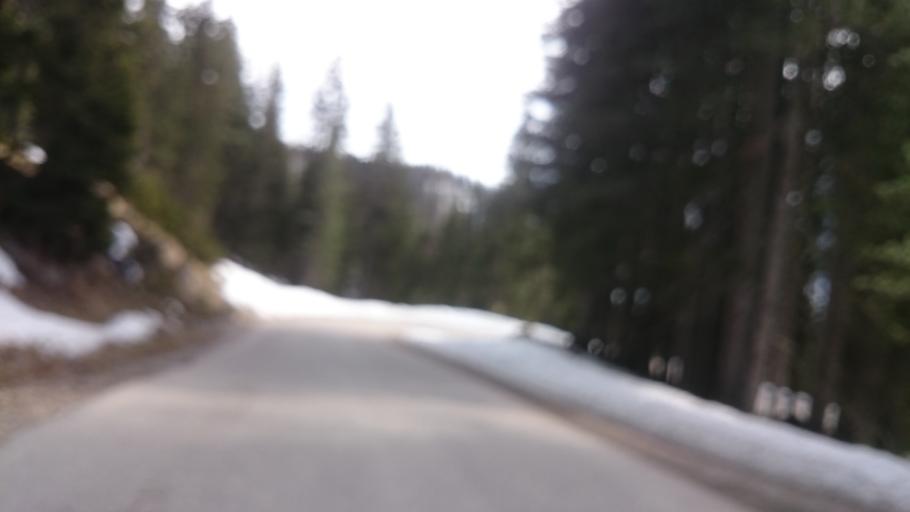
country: IT
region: Trentino-Alto Adige
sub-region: Bolzano
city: Braies
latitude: 46.6600
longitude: 12.1680
